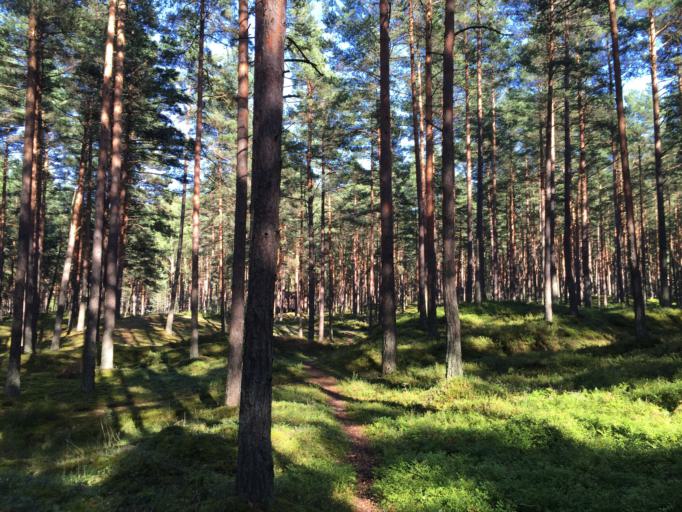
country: LV
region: Riga
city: Jaunciems
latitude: 57.0835
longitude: 24.1416
